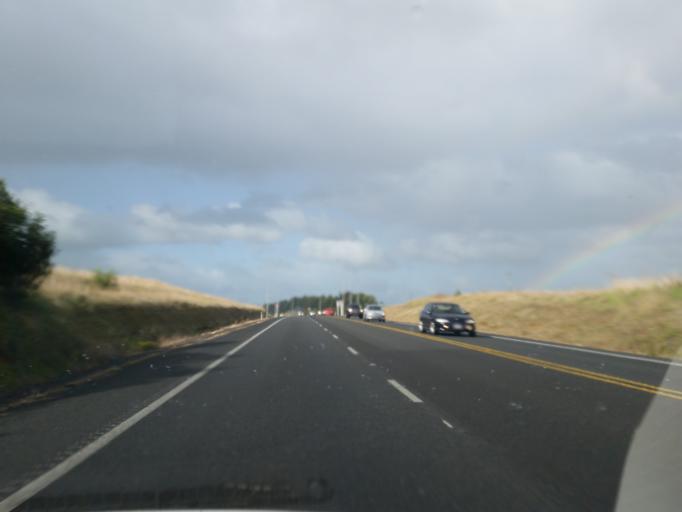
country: NZ
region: Auckland
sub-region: Auckland
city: Pukekohe East
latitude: -37.2194
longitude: 175.1150
